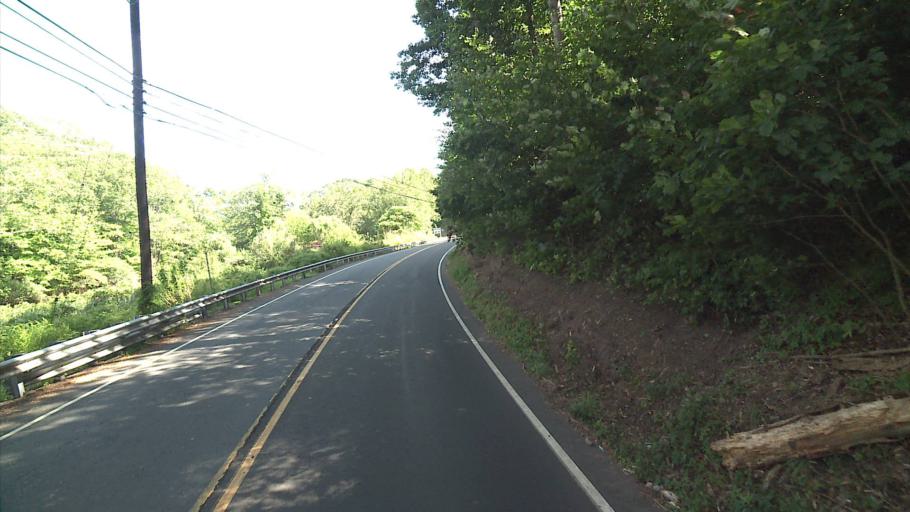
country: US
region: Connecticut
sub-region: New Haven County
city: Meriden
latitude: 41.5239
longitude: -72.8400
